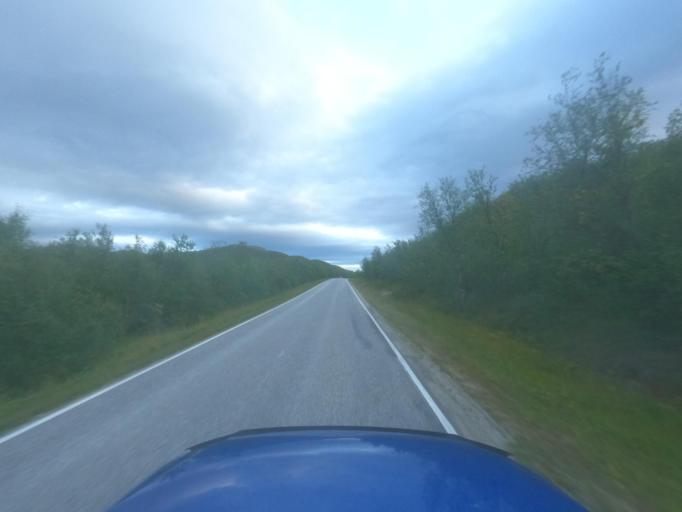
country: NO
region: Finnmark Fylke
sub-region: Porsanger
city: Lakselv
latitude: 69.9686
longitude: 24.9703
